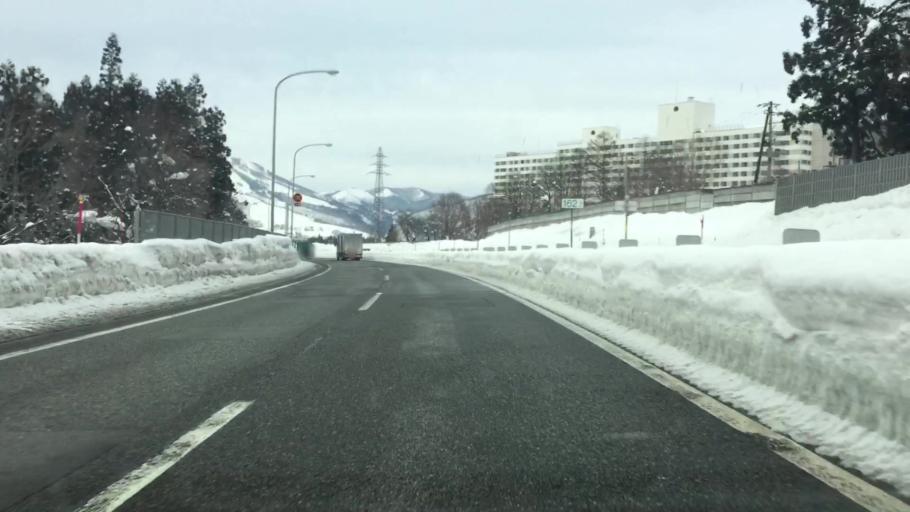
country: JP
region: Niigata
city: Shiozawa
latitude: 36.9018
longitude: 138.8476
